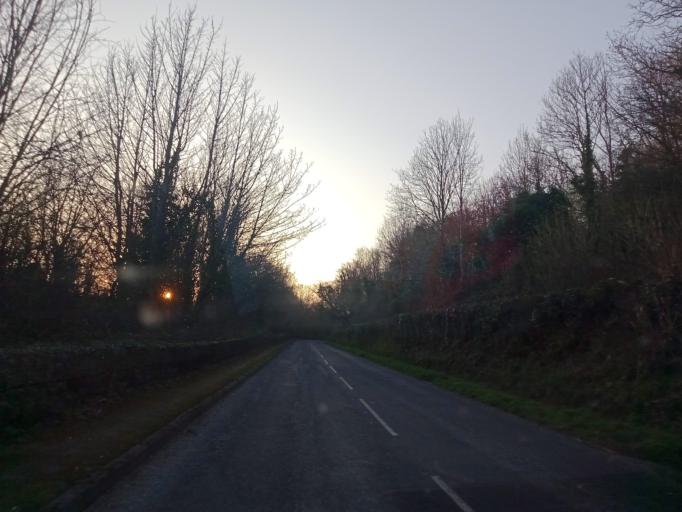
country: IE
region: Leinster
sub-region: Kilkenny
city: Castlecomer
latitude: 52.8079
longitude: -7.2197
